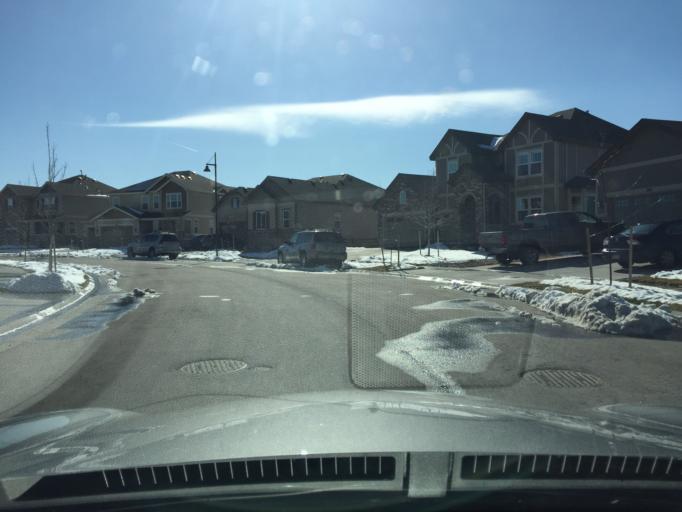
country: US
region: Colorado
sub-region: Boulder County
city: Erie
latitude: 40.0450
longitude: -105.0399
